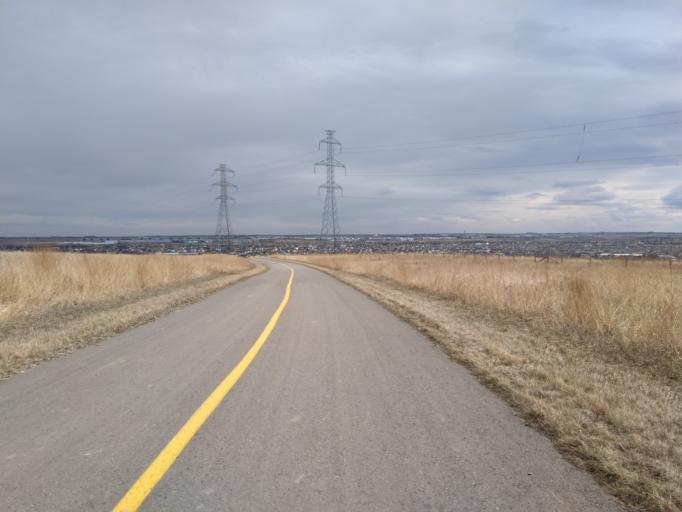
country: CA
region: Alberta
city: Calgary
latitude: 51.1750
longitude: -114.0651
